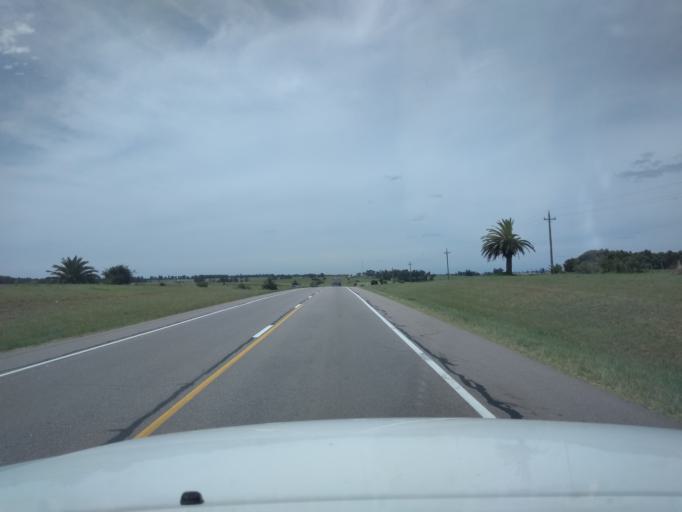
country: UY
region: Florida
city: Florida
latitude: -34.2266
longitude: -56.2111
